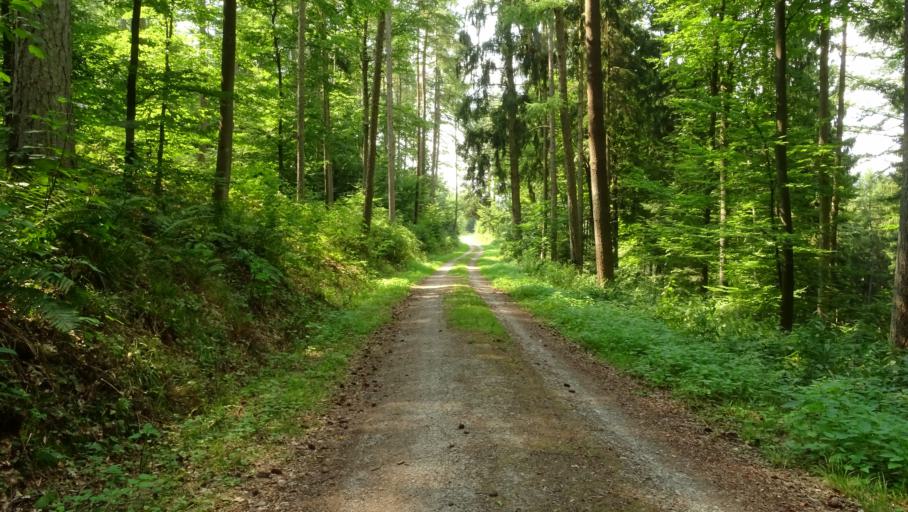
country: DE
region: Baden-Wuerttemberg
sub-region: Karlsruhe Region
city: Neckargerach
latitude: 49.4031
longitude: 9.0981
